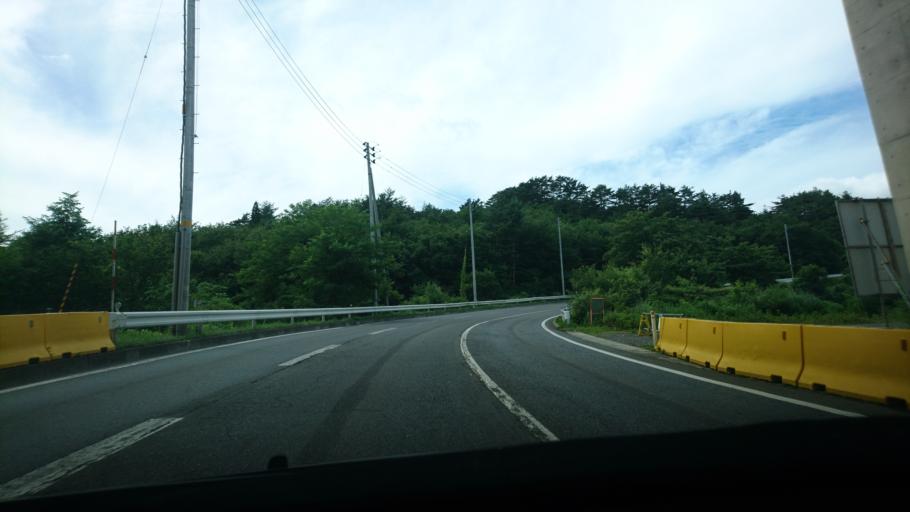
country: JP
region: Aomori
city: Hachinohe
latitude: 40.2306
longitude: 141.7811
